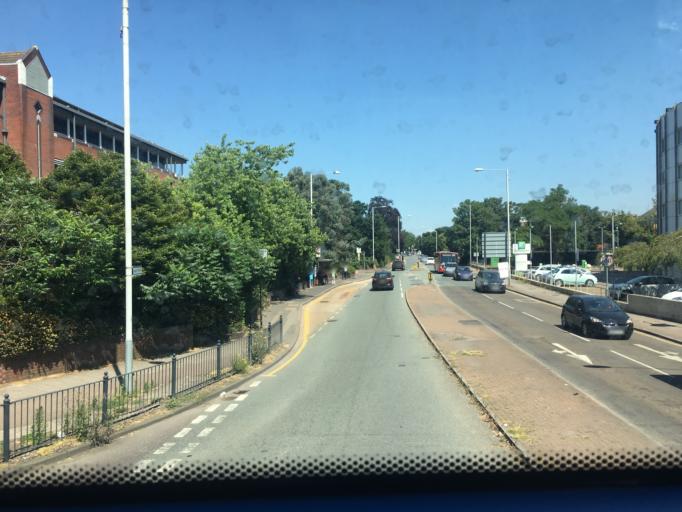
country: GB
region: England
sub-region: Greater London
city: Hayes
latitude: 51.4808
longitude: -0.4344
